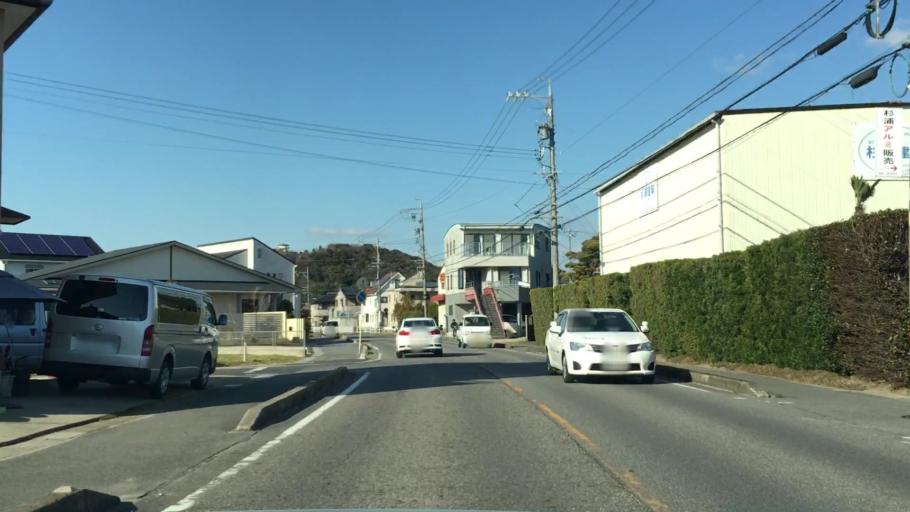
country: JP
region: Aichi
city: Nishio
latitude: 34.8680
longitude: 137.0737
